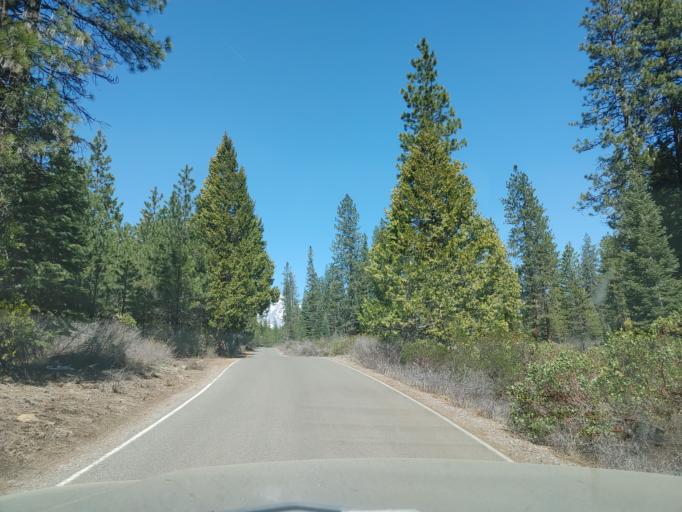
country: US
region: California
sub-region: Siskiyou County
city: McCloud
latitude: 41.2426
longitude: -122.0263
